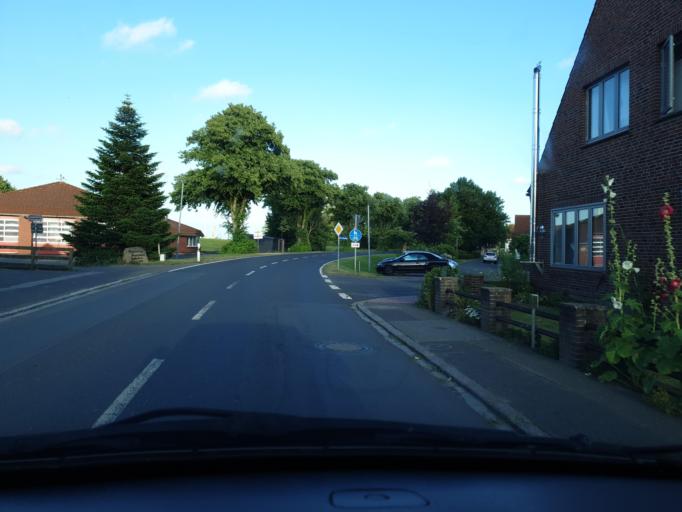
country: DE
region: Schleswig-Holstein
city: Wohrden
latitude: 54.1651
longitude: 9.0011
